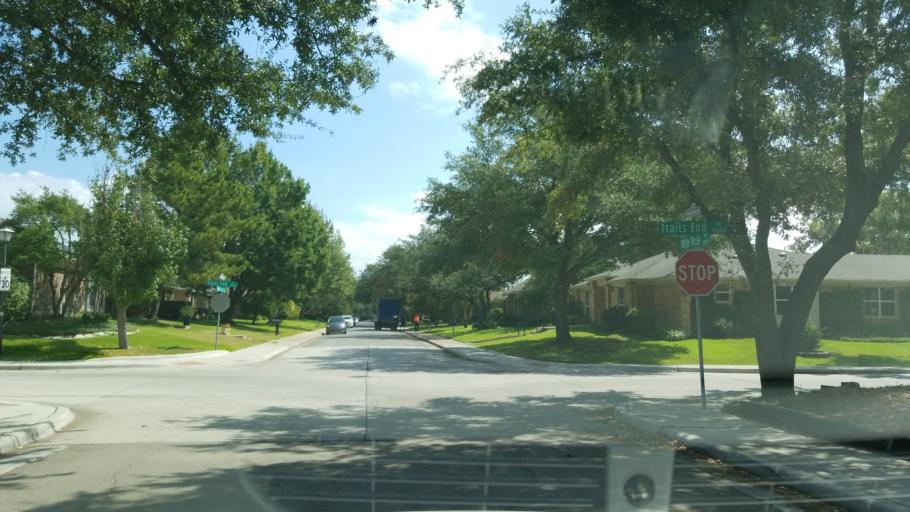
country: US
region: Texas
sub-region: Dallas County
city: Addison
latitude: 32.9572
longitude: -96.8026
